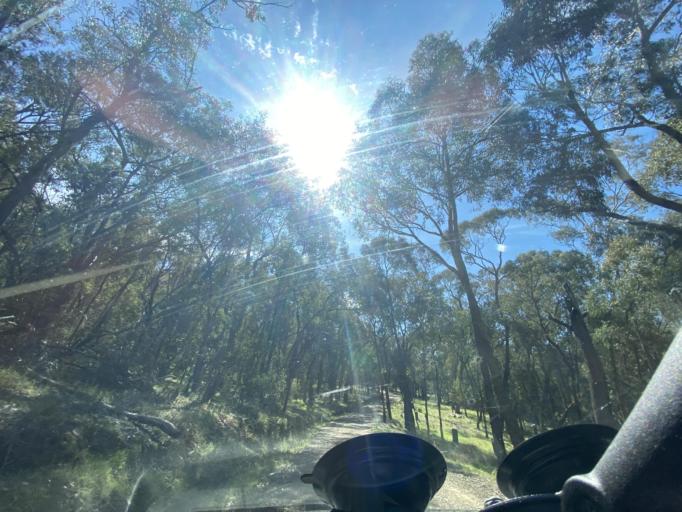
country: AU
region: Victoria
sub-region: Mansfield
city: Mansfield
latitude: -36.8038
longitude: 146.1215
